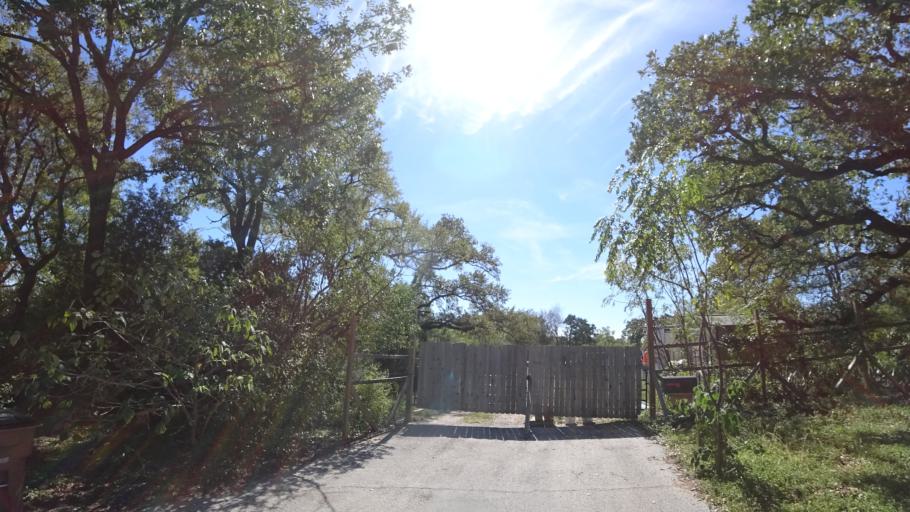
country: US
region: Texas
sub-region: Travis County
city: Austin
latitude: 30.2731
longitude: -97.6823
